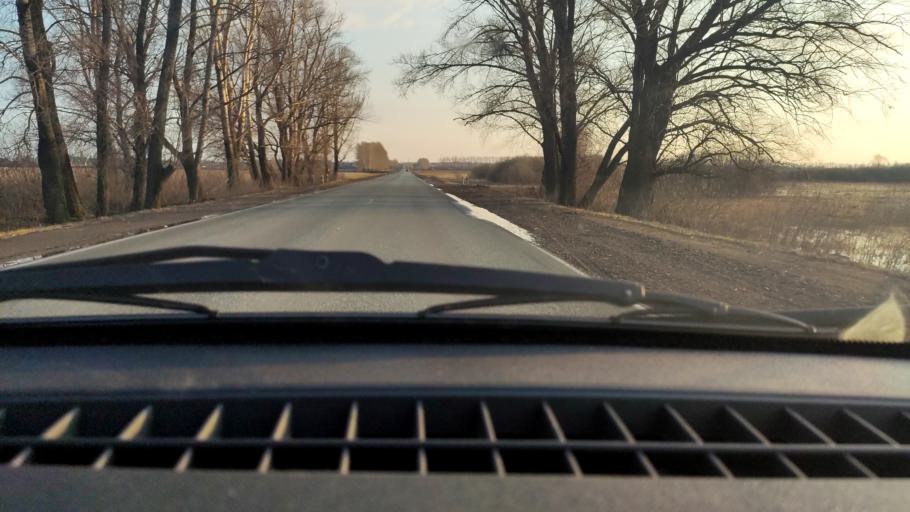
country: RU
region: Bashkortostan
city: Chishmy
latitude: 54.4024
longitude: 55.2142
